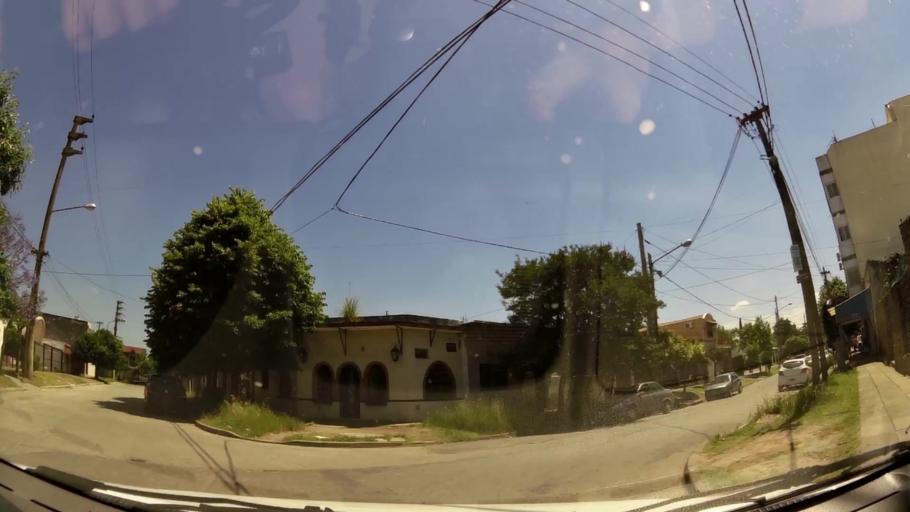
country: AR
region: Buenos Aires
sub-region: Partido de Merlo
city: Merlo
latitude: -34.6620
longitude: -58.6922
